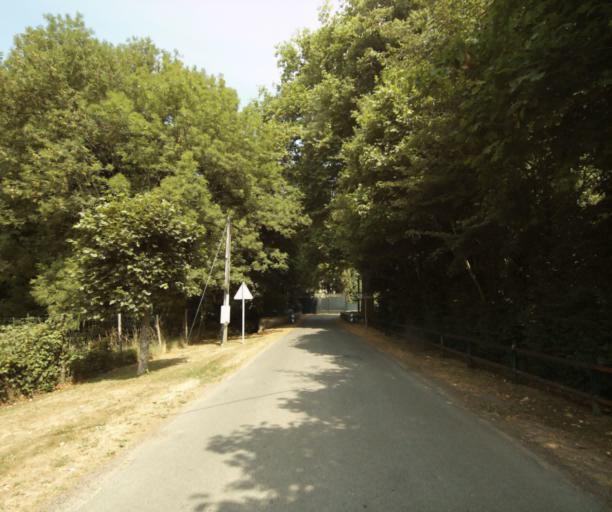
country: FR
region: Centre
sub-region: Departement d'Eure-et-Loir
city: Authon-du-Perche
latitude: 48.1901
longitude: 0.9343
